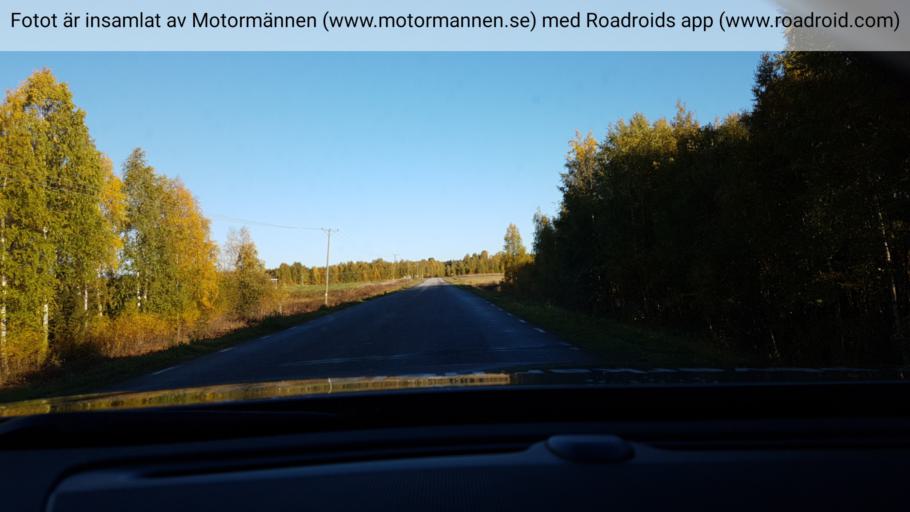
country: SE
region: Norrbotten
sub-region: Bodens Kommun
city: Boden
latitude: 65.8793
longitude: 21.6786
